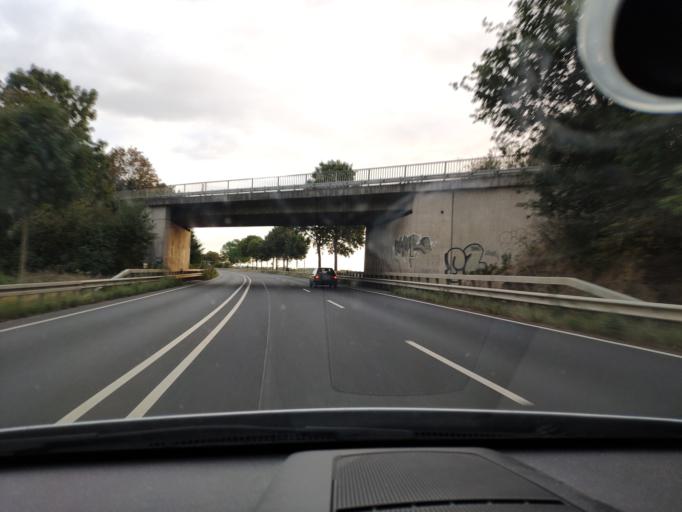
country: DE
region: North Rhine-Westphalia
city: Geilenkirchen
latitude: 50.9903
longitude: 6.1013
